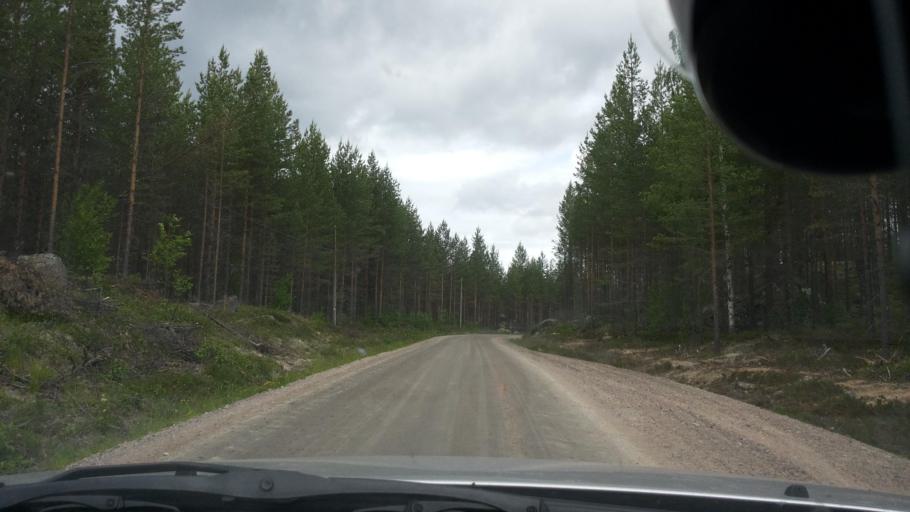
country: SE
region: Gaevleborg
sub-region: Ovanakers Kommun
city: Edsbyn
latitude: 61.5181
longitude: 15.3541
